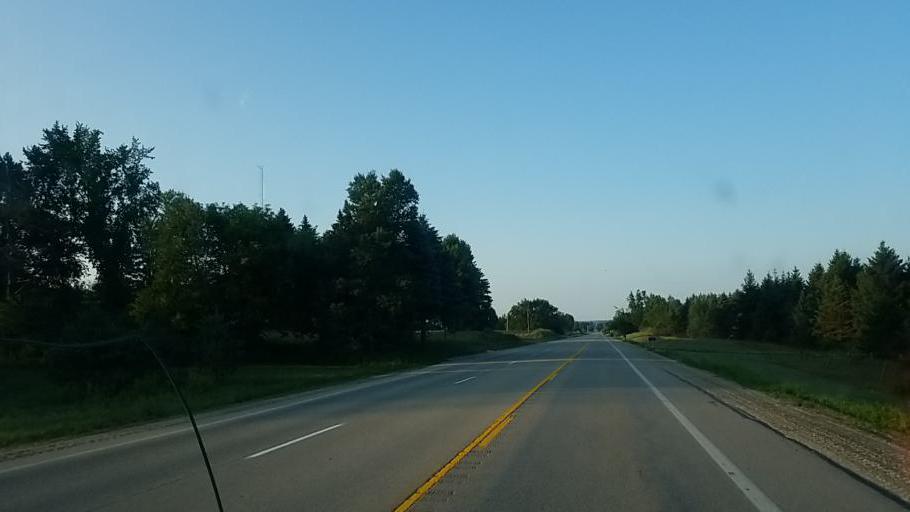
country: US
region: Michigan
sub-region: Isabella County
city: Lake Isabella
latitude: 43.6745
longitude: -85.1464
